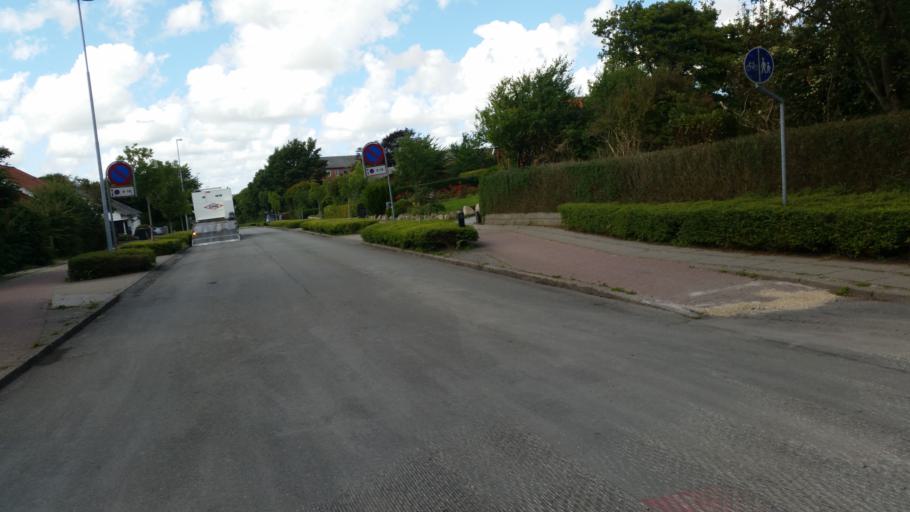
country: DK
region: North Denmark
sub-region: Thisted Kommune
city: Thisted
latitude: 56.9587
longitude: 8.6972
